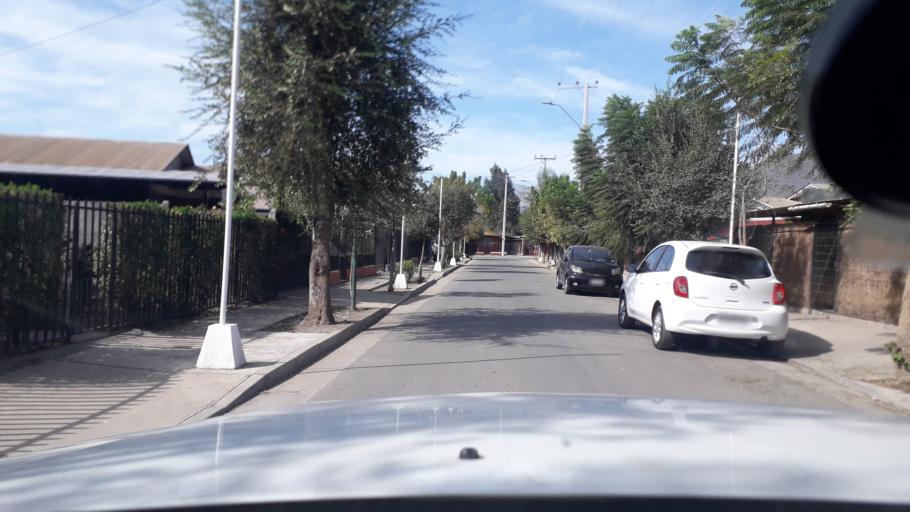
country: CL
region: Valparaiso
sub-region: Provincia de San Felipe
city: Llaillay
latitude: -32.8022
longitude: -70.9059
